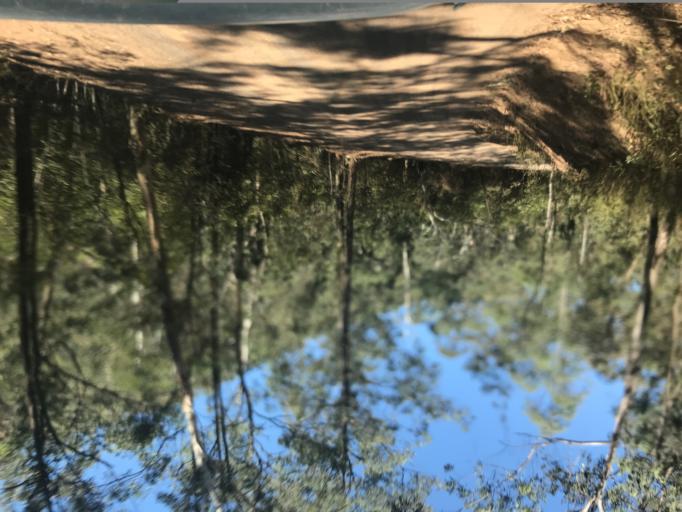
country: AU
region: New South Wales
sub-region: Wyong Shire
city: Little Jilliby
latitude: -33.1820
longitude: 151.0551
